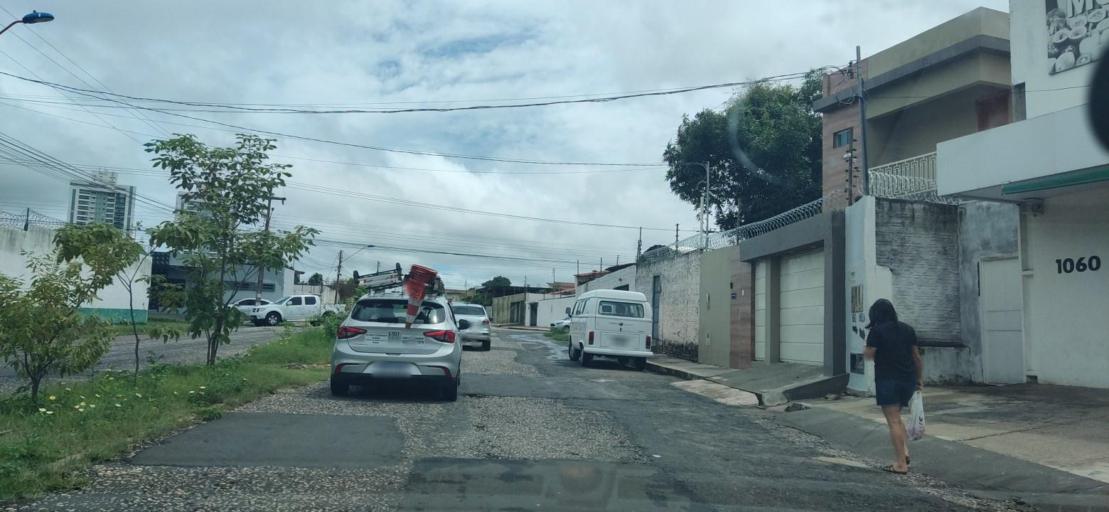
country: BR
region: Piaui
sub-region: Teresina
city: Teresina
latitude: -5.0717
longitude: -42.7689
